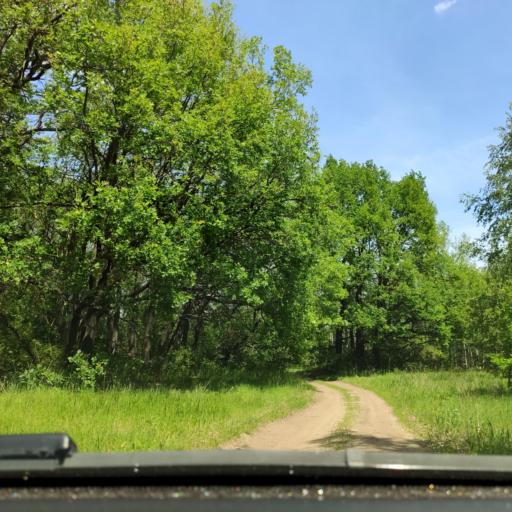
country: RU
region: Voronezj
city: Podgornoye
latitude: 51.8064
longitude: 39.1496
